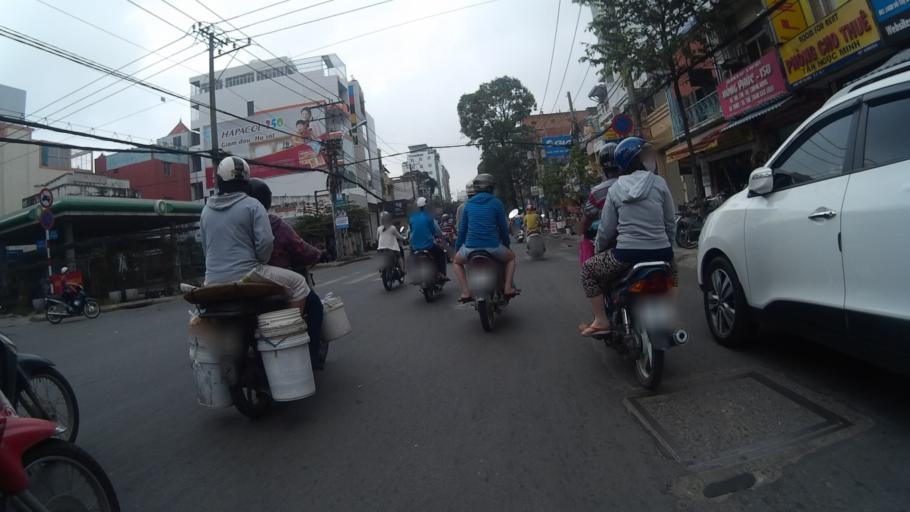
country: VN
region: Ho Chi Minh City
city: Quan Mot
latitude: 10.7871
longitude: 106.6912
